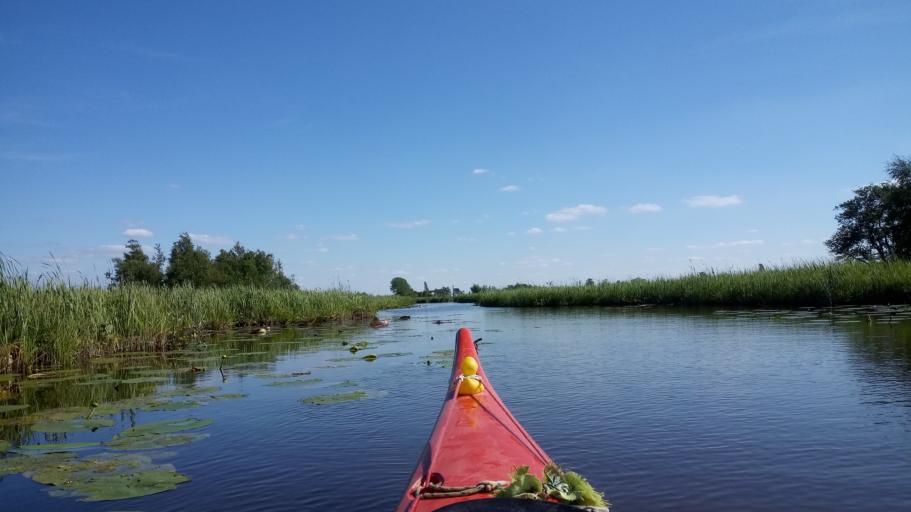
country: NL
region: South Holland
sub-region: Gemeente Nieuwkoop
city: Nieuwkoop
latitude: 52.1490
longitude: 4.8227
